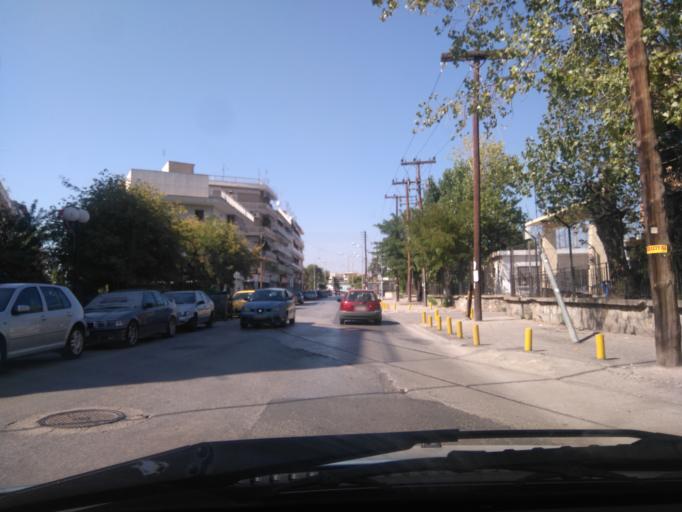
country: GR
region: Central Macedonia
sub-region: Nomos Thessalonikis
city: Evosmos
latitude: 40.6589
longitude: 22.9135
